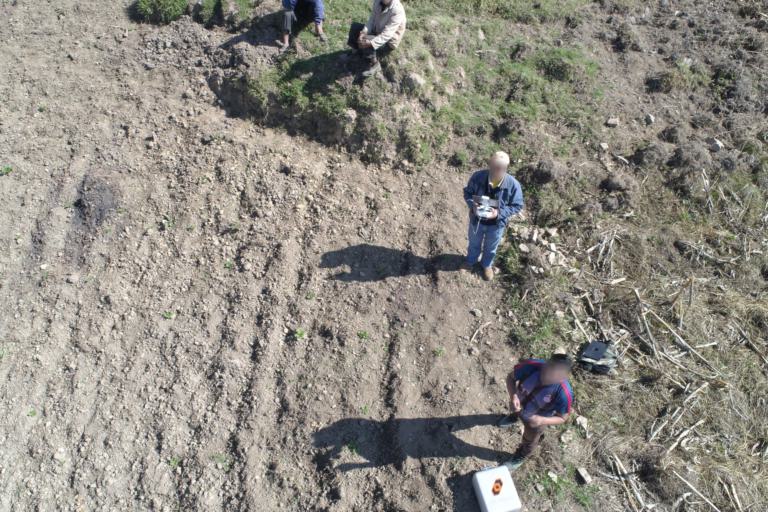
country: BO
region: La Paz
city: Amarete
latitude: -15.4976
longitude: -68.8745
